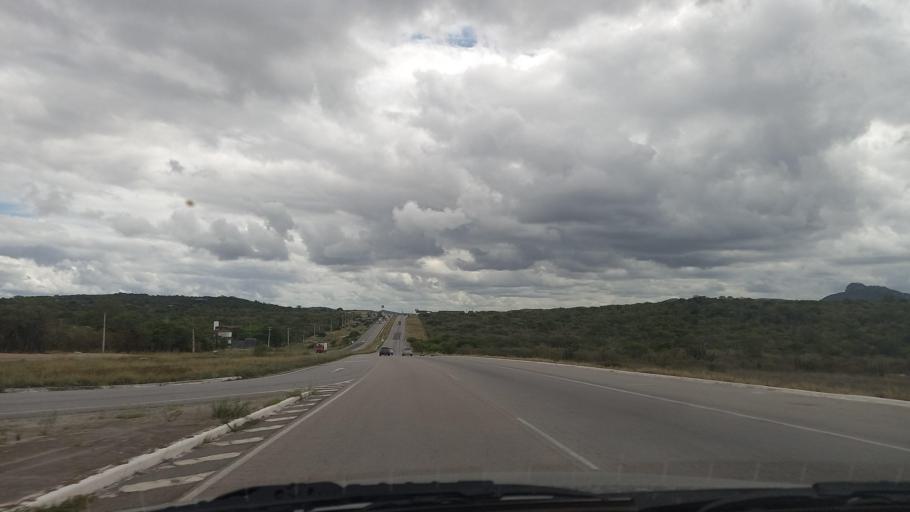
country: BR
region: Pernambuco
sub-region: Caruaru
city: Caruaru
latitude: -8.3195
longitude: -36.0686
